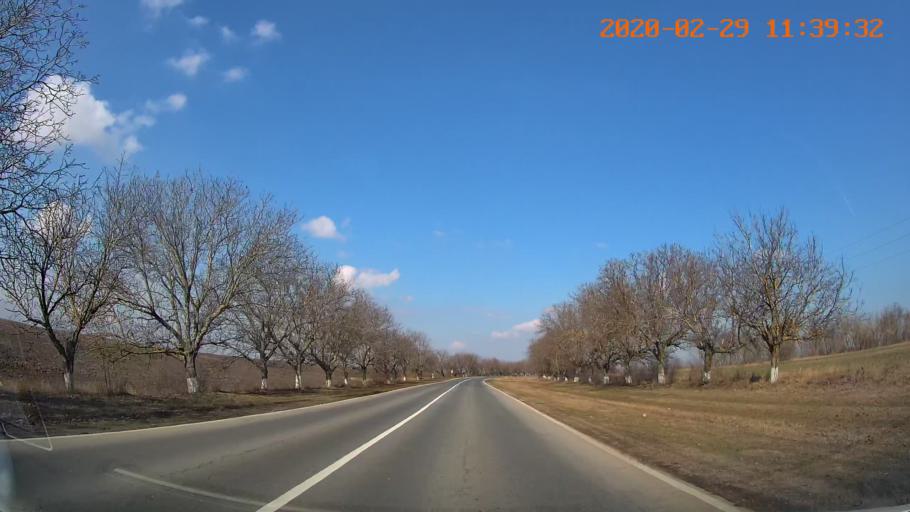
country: MD
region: Rezina
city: Saharna
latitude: 47.6415
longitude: 29.0244
